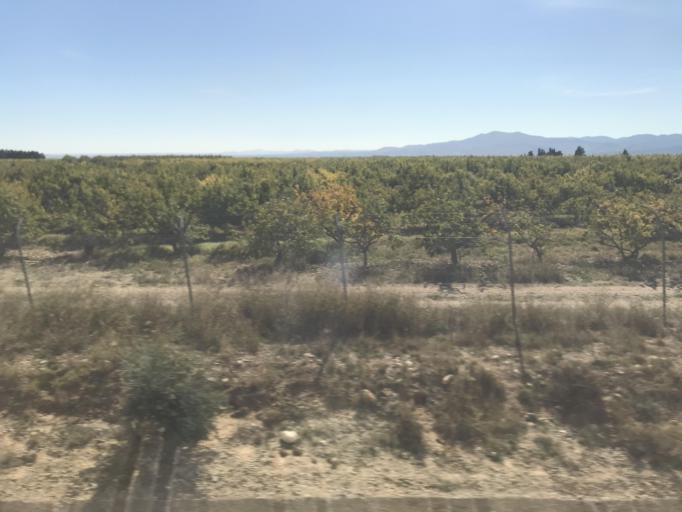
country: ES
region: Aragon
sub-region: Provincia de Zaragoza
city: Calatorao
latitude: 41.5331
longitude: -1.3794
